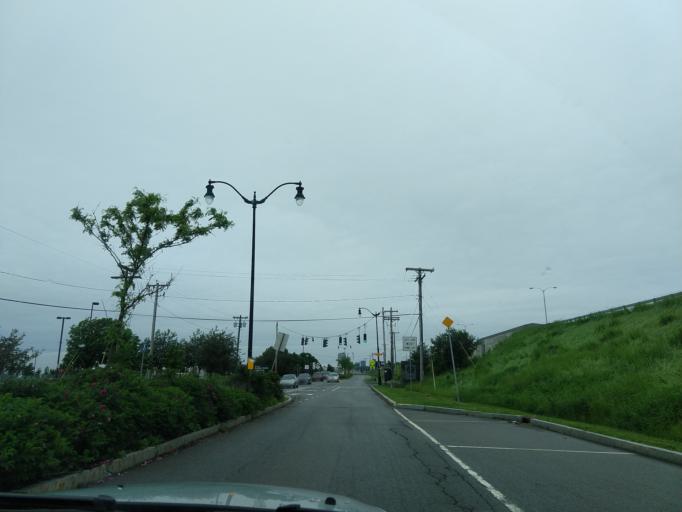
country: US
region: New York
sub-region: Erie County
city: Lackawanna
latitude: 42.8454
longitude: -78.8606
